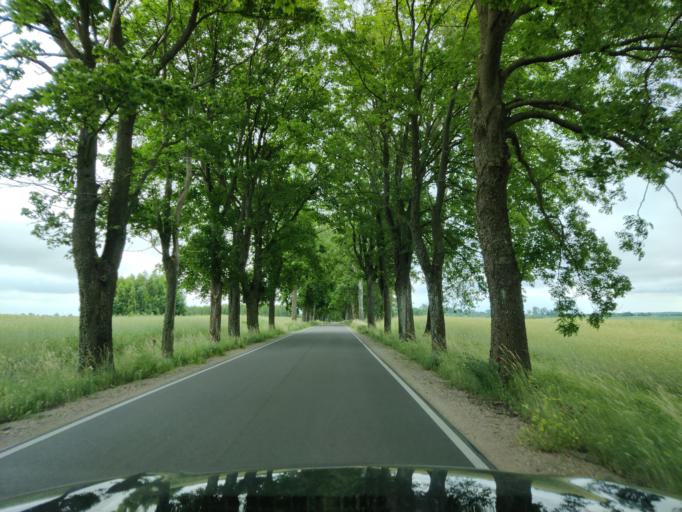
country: PL
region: Warmian-Masurian Voivodeship
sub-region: Powiat mragowski
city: Mikolajki
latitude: 53.8586
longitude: 21.6080
